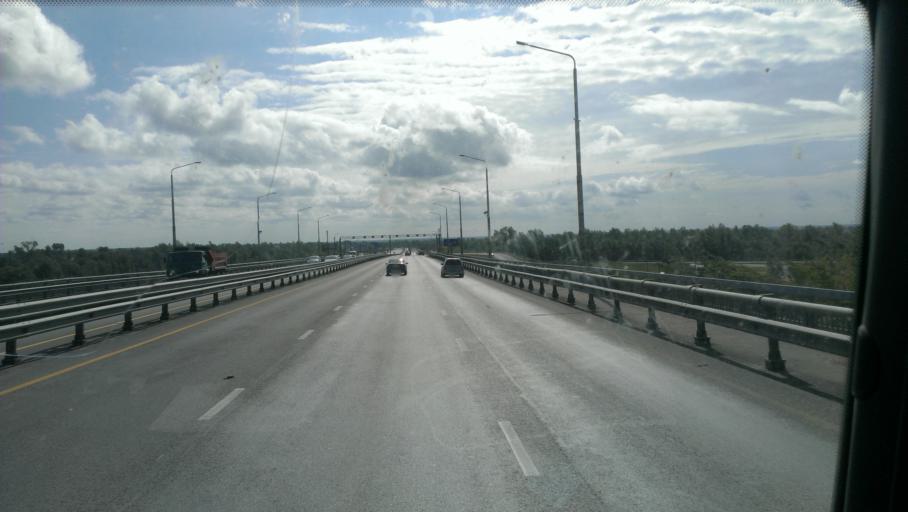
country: RU
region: Altai Krai
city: Zaton
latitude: 53.3215
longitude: 83.8082
